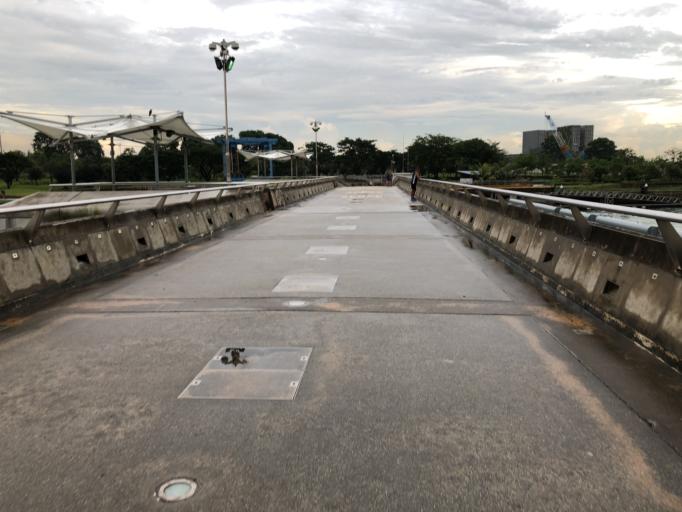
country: SG
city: Singapore
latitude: 1.2817
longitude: 103.8730
